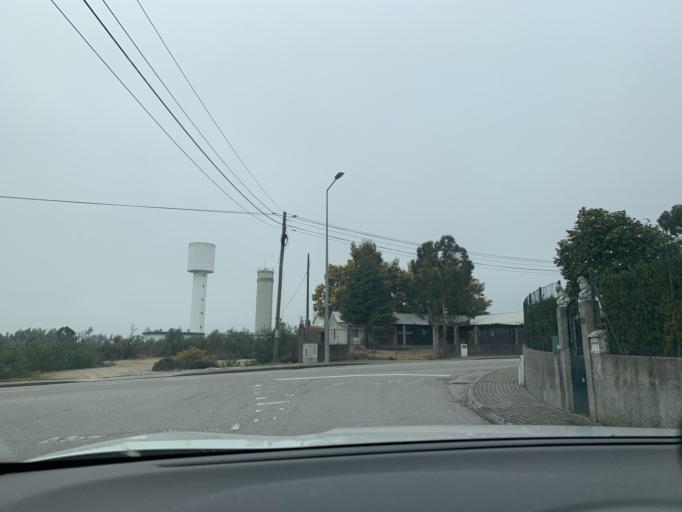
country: PT
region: Viseu
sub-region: Concelho de Tondela
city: Tondela
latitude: 40.5031
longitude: -8.0790
